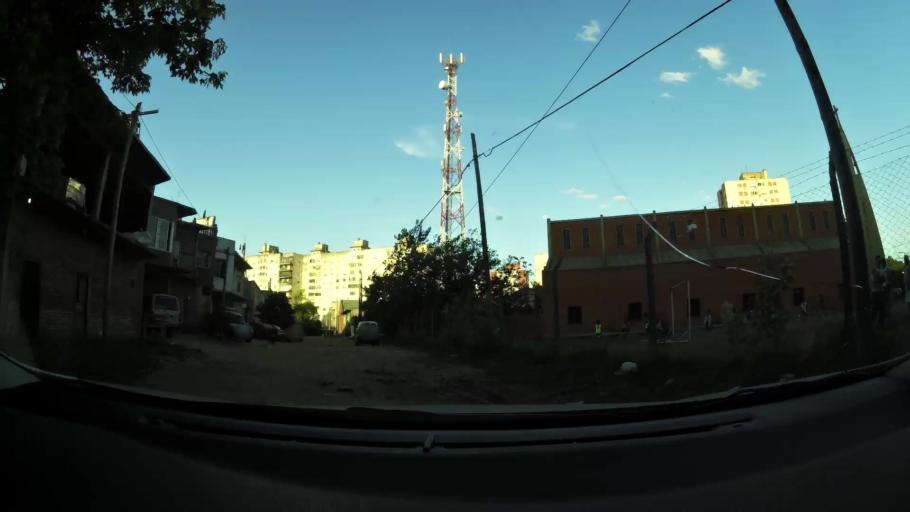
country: AR
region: Buenos Aires F.D.
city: Villa Lugano
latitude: -34.6968
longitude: -58.4792
